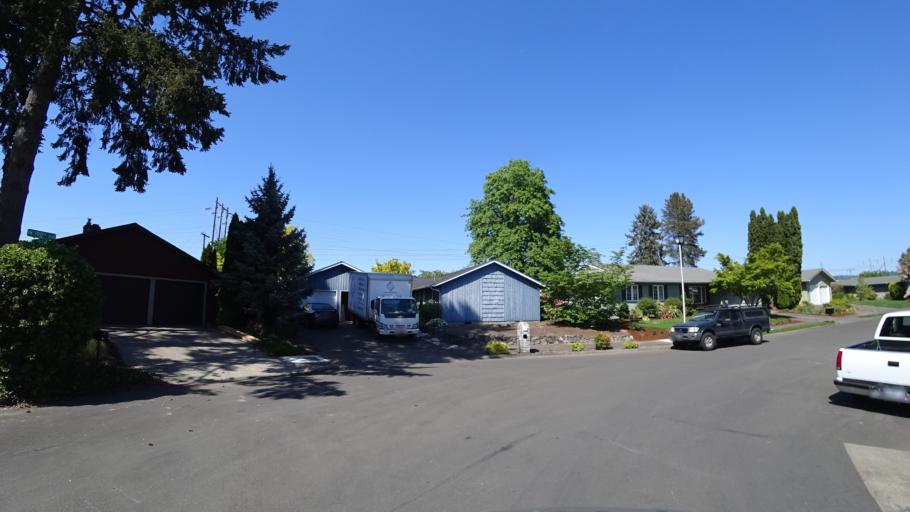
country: US
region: Oregon
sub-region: Washington County
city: Bethany
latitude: 45.5555
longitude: -122.8720
